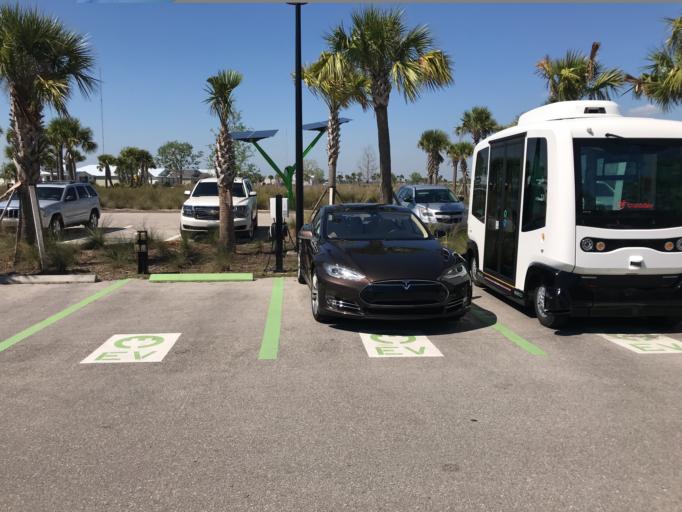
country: US
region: Florida
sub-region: Lee County
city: Olga
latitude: 26.7840
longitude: -81.7480
